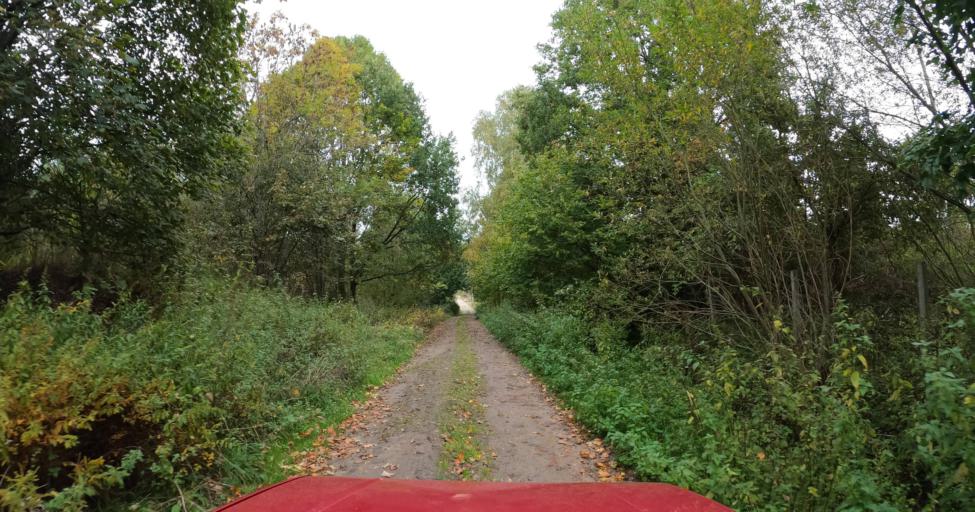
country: PL
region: West Pomeranian Voivodeship
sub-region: Powiat koszalinski
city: Bobolice
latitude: 54.1124
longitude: 16.5085
